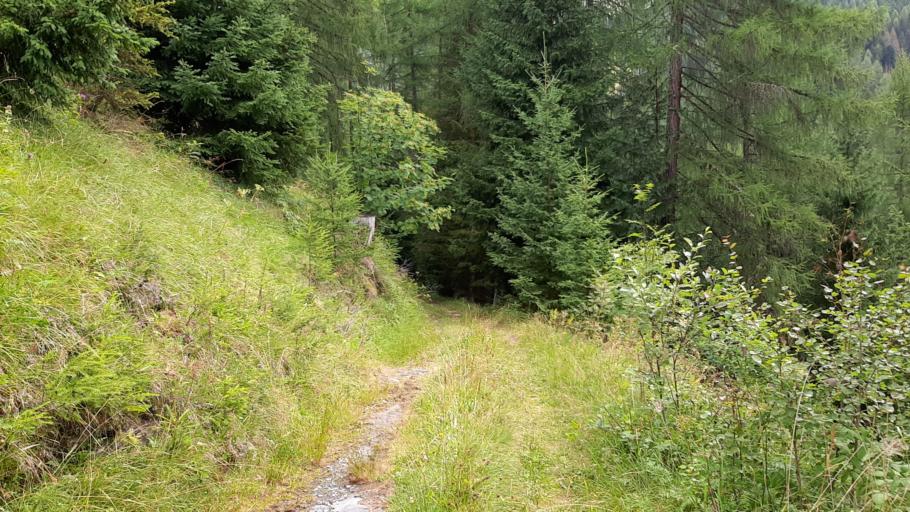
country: IT
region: Trentino-Alto Adige
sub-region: Bolzano
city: Sesto
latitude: 46.6964
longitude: 12.3763
